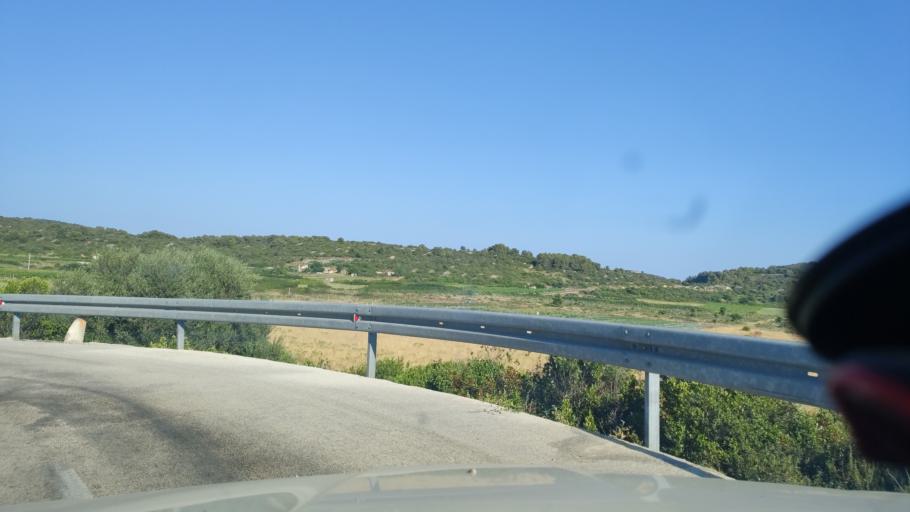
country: HR
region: Splitsko-Dalmatinska
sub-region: Grad Vis
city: Vis
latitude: 43.0426
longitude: 16.1958
